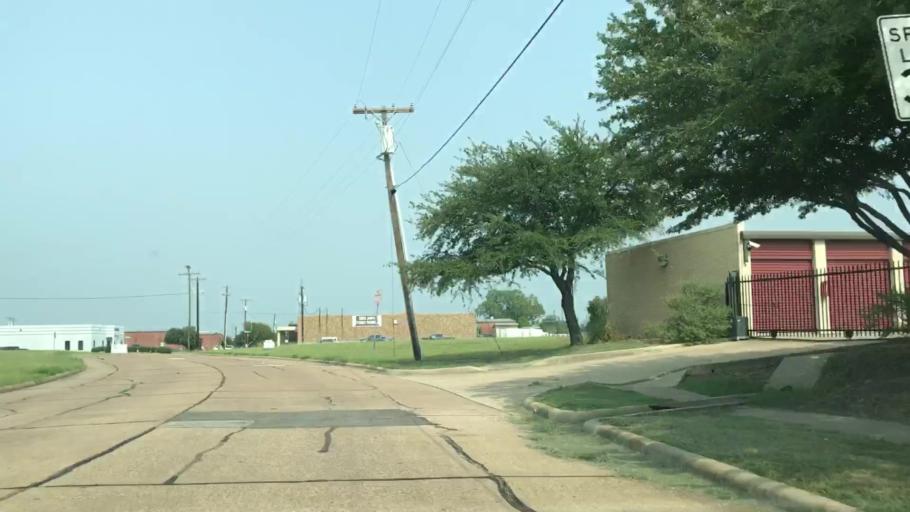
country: US
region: Texas
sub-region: Dallas County
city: Rowlett
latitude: 32.9047
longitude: -96.5679
